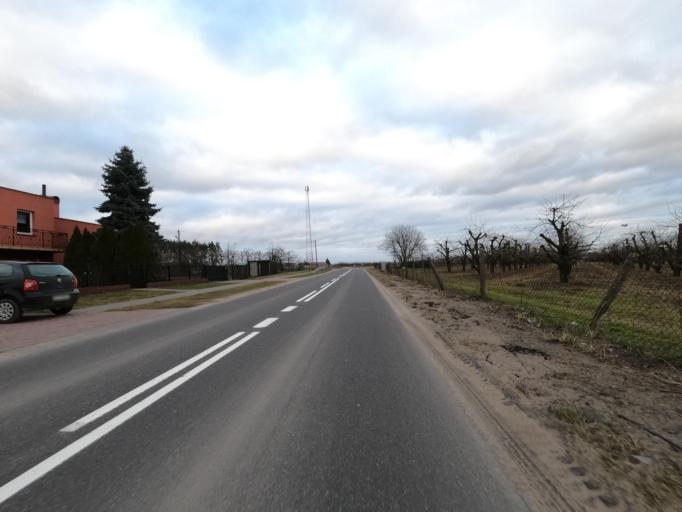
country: PL
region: Greater Poland Voivodeship
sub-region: Powiat pilski
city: Bialosliwie
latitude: 53.1096
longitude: 17.1319
